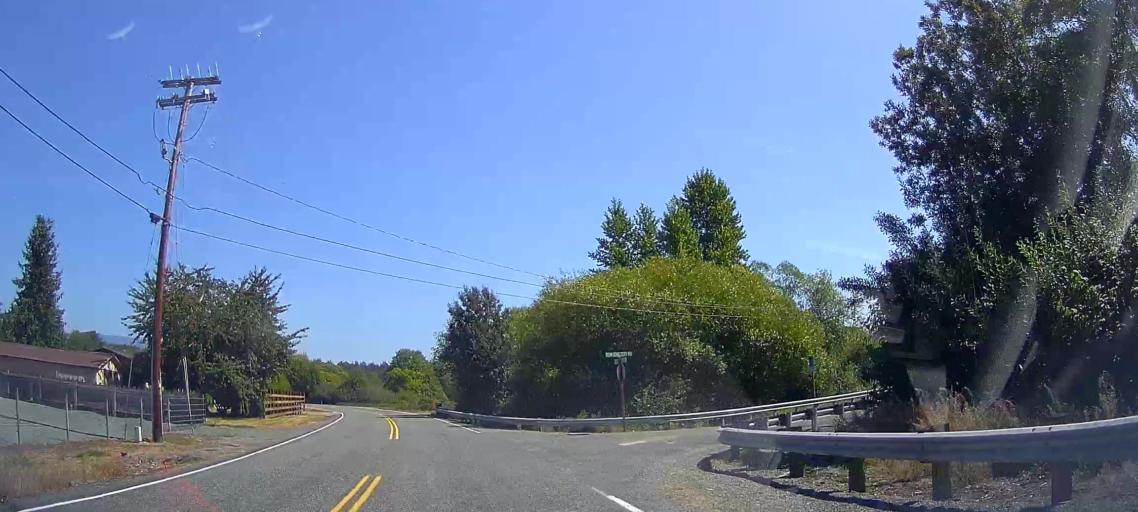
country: US
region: Washington
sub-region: Skagit County
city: Burlington
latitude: 48.5577
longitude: -122.4066
